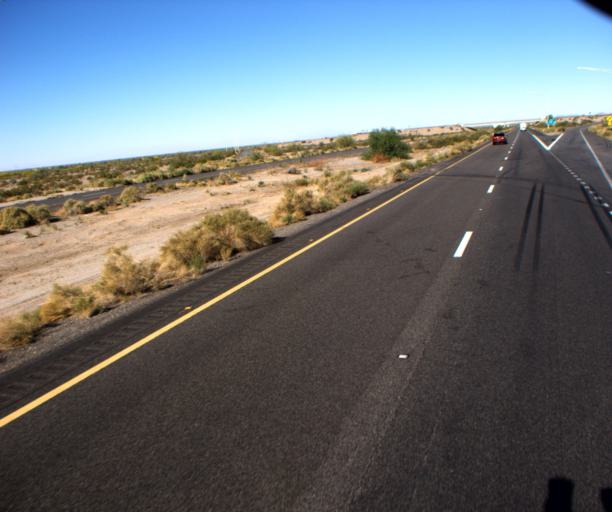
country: US
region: Arizona
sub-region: Maricopa County
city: Gila Bend
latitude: 32.9240
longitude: -112.6648
